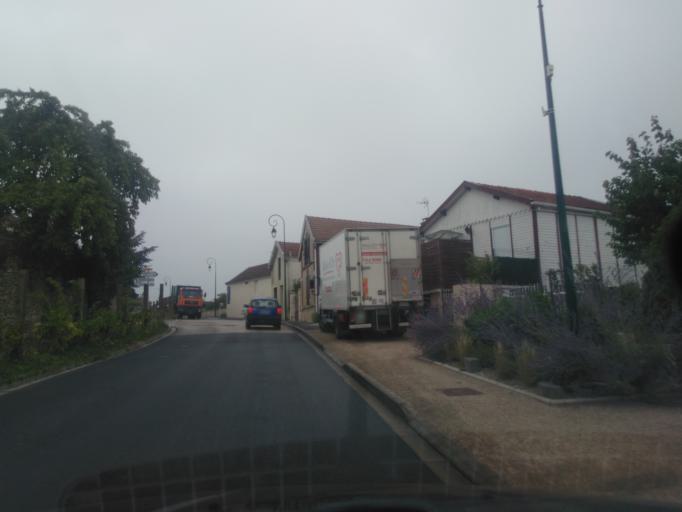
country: FR
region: Champagne-Ardenne
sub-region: Departement de la Marne
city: Mardeuil
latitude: 49.0728
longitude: 3.9318
